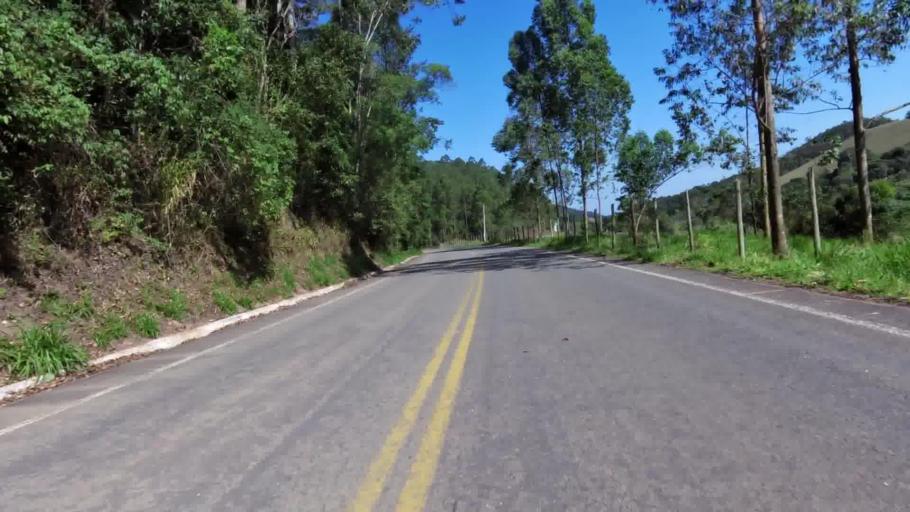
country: BR
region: Espirito Santo
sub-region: Alfredo Chaves
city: Alfredo Chaves
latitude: -20.5368
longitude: -40.7870
